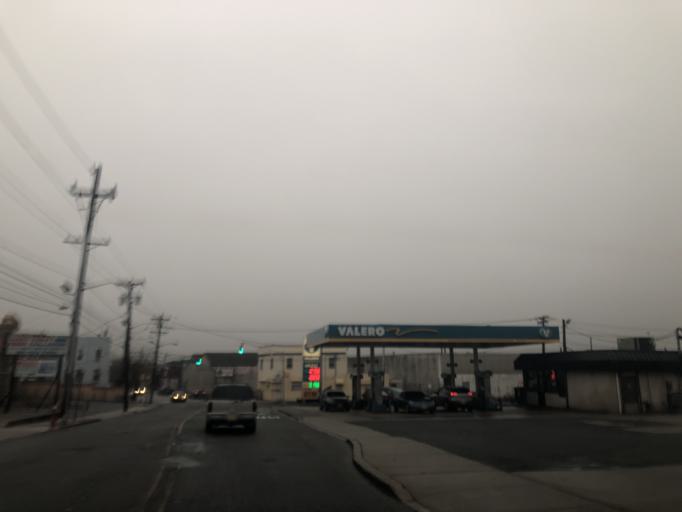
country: US
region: New Jersey
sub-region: Hudson County
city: Jersey City
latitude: 40.7056
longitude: -74.0740
